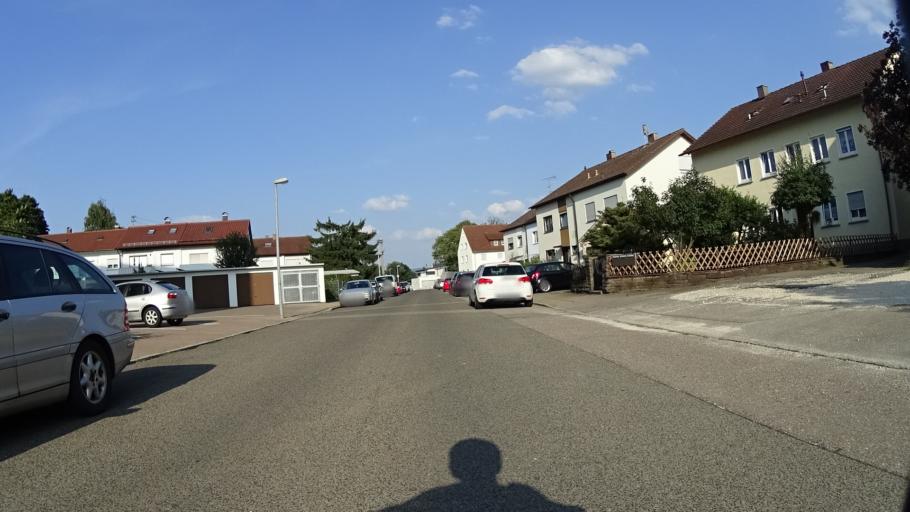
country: DE
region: Baden-Wuerttemberg
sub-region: Regierungsbezirk Stuttgart
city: Eislingen
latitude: 48.6902
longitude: 9.6834
